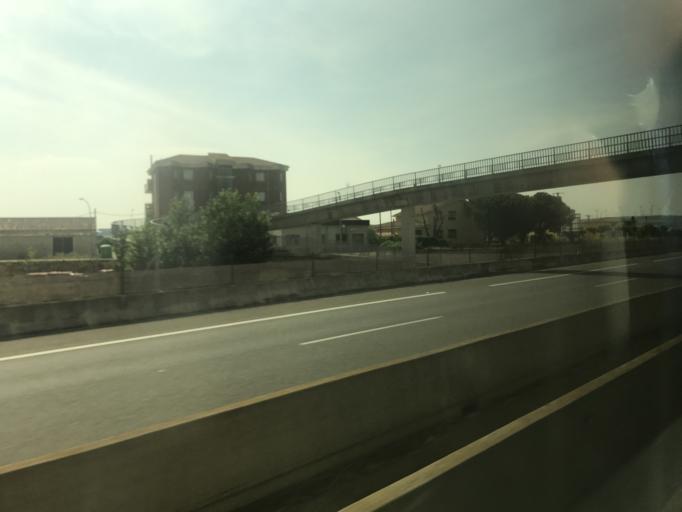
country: ES
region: Castille and Leon
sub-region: Provincia de Palencia
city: Quintana del Puente
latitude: 42.0835
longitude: -4.2099
